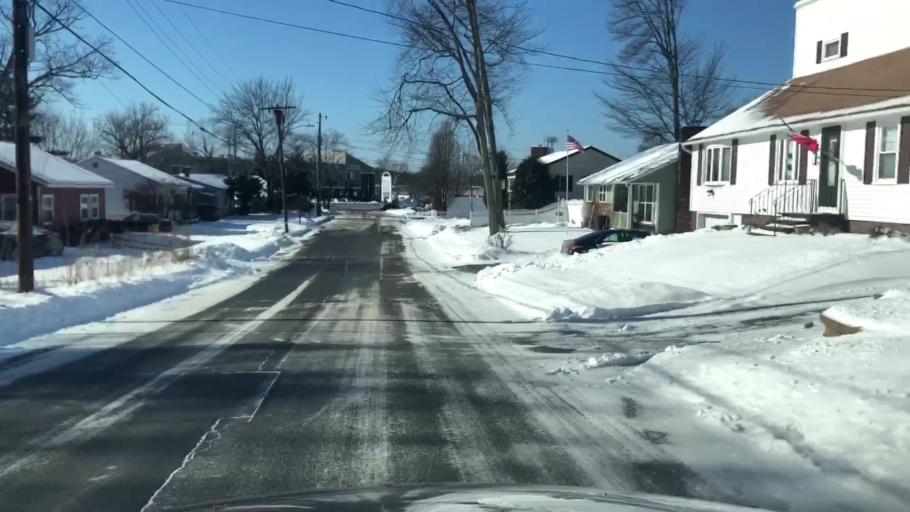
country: US
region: New Hampshire
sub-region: Hillsborough County
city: Manchester
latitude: 42.9662
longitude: -71.4470
